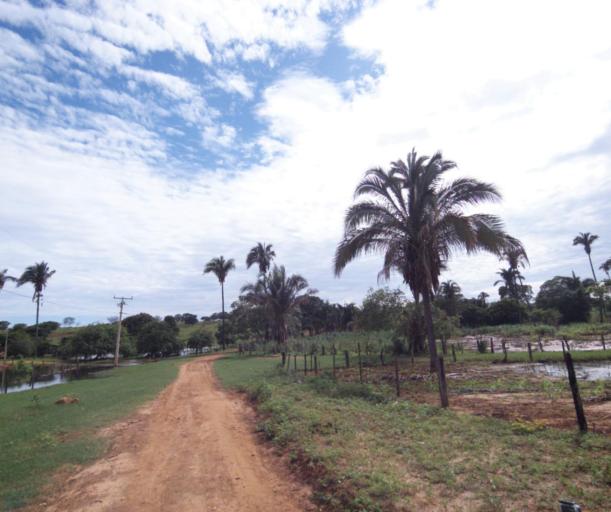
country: BR
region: Bahia
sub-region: Carinhanha
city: Carinhanha
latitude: -14.2372
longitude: -44.4074
